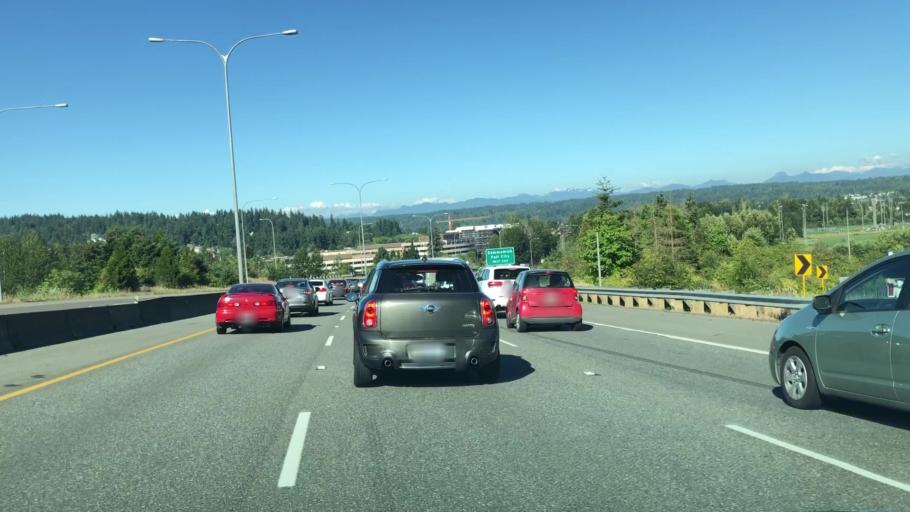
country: US
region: Washington
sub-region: King County
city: Redmond
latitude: 47.6653
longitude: -122.1300
